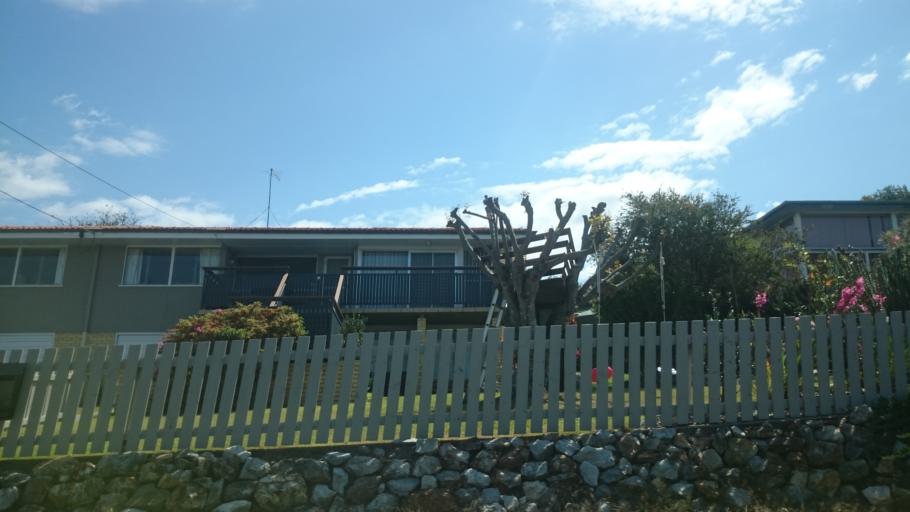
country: AU
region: Queensland
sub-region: Brisbane
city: Manly West
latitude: -27.4652
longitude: 153.1744
